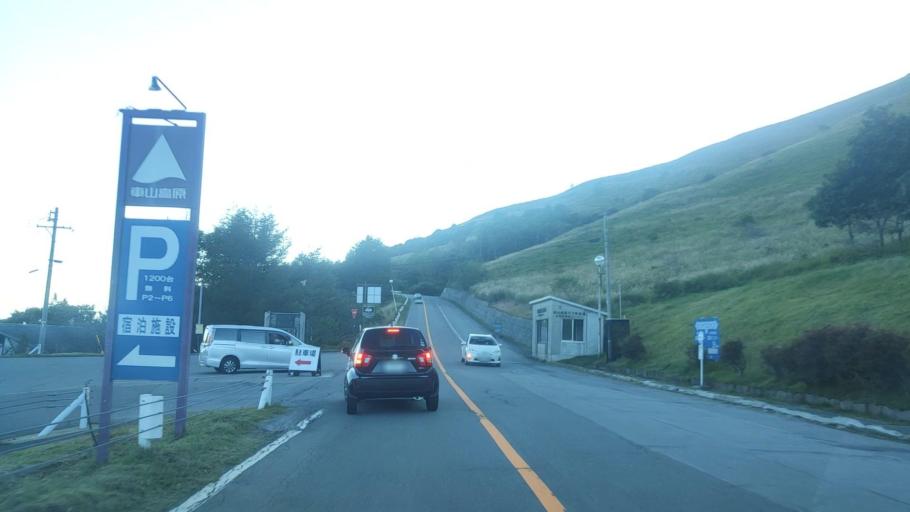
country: JP
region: Nagano
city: Suwa
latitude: 36.1011
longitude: 138.2114
